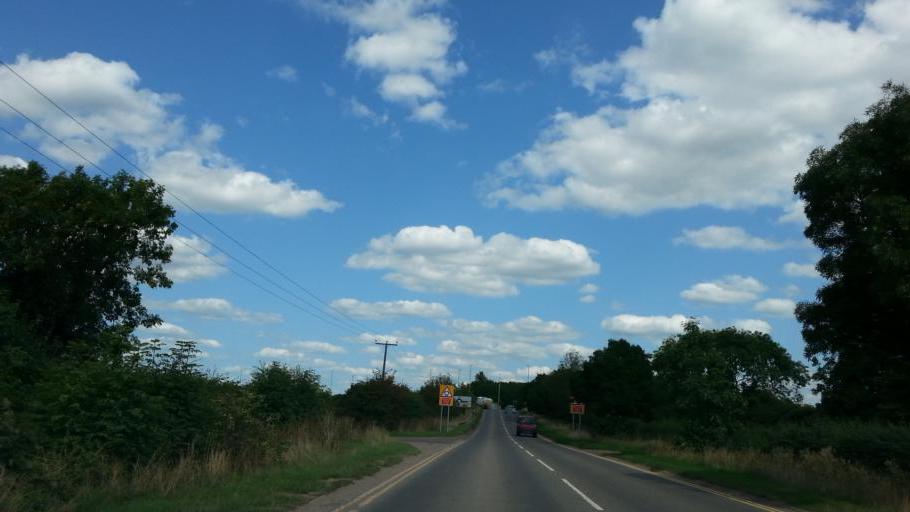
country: GB
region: England
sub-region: Leicestershire
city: Barrow upon Soar
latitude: 52.7391
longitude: -1.1476
